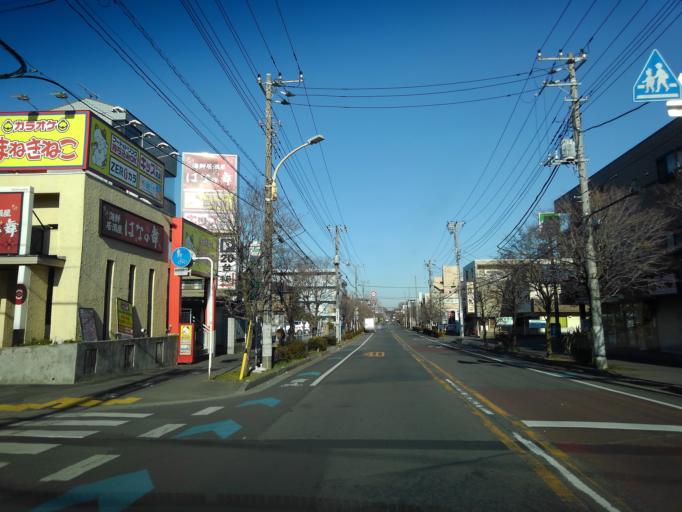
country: JP
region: Saitama
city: Tokorozawa
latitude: 35.7954
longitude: 139.5129
